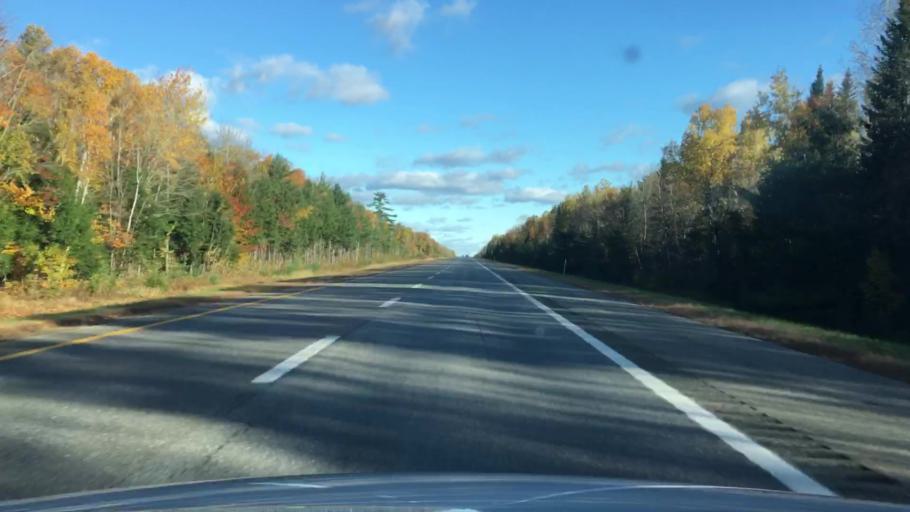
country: US
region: Maine
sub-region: Penobscot County
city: Greenbush
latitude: 45.0714
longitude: -68.6905
